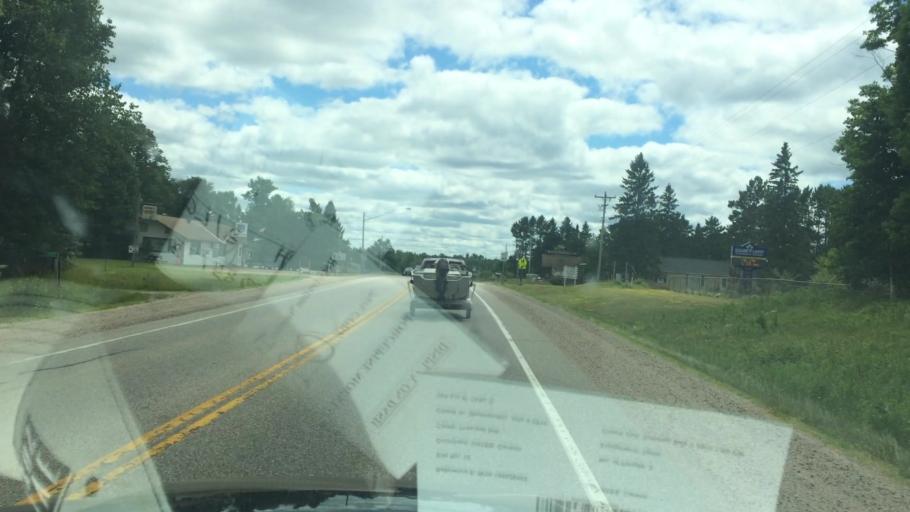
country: US
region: Wisconsin
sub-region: Vilas County
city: Eagle River
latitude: 45.7910
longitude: -89.3209
